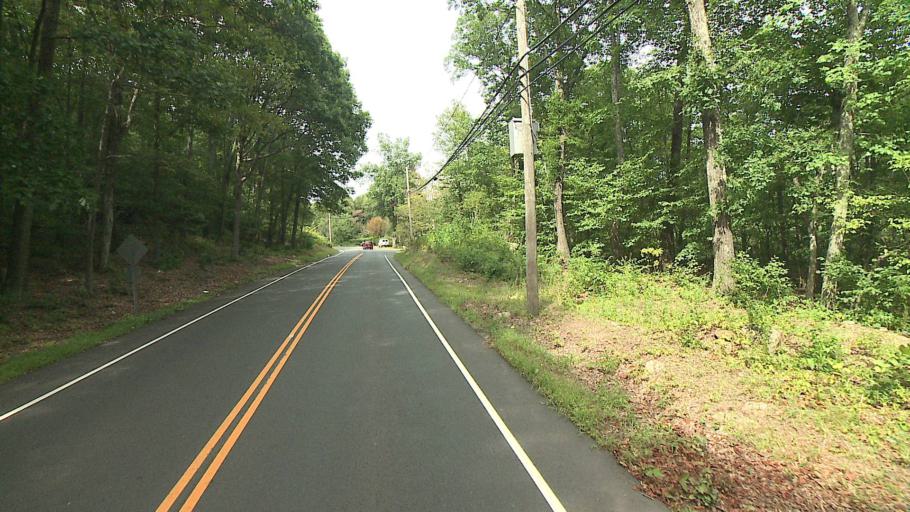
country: US
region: Connecticut
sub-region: Litchfield County
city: Plymouth
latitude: 41.6628
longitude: -73.0484
